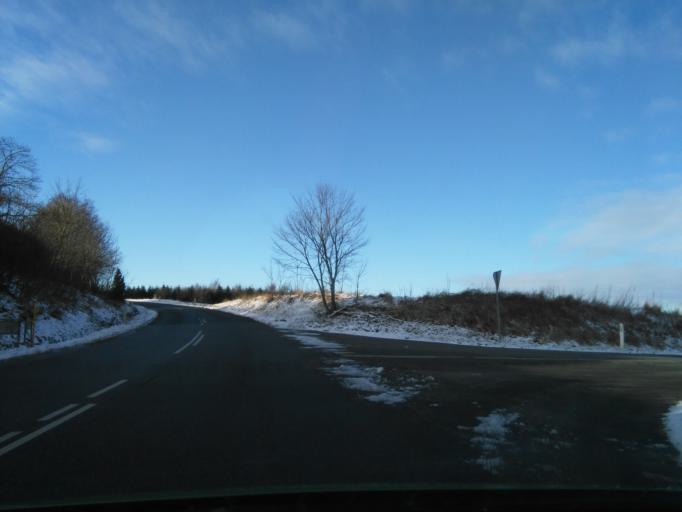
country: DK
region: Central Jutland
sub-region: Arhus Kommune
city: Framlev
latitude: 56.1194
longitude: 9.9882
